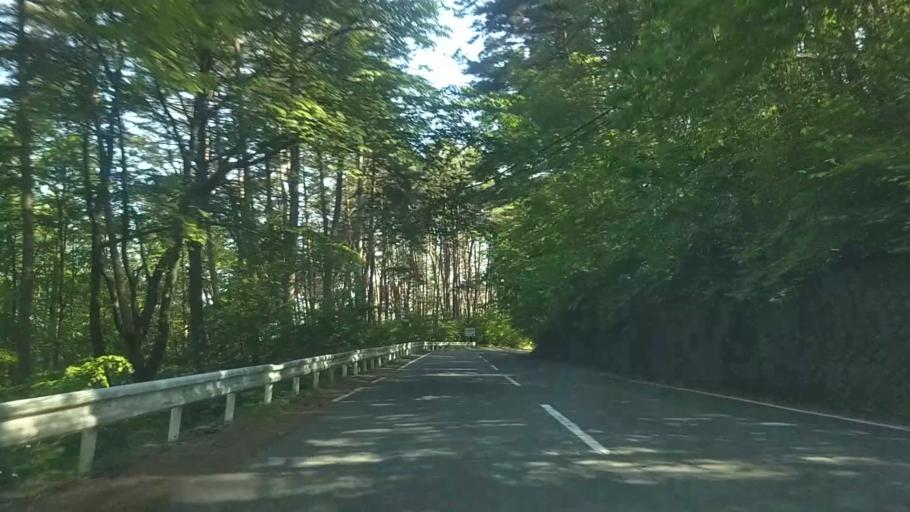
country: JP
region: Yamanashi
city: Nirasaki
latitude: 35.8887
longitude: 138.3899
